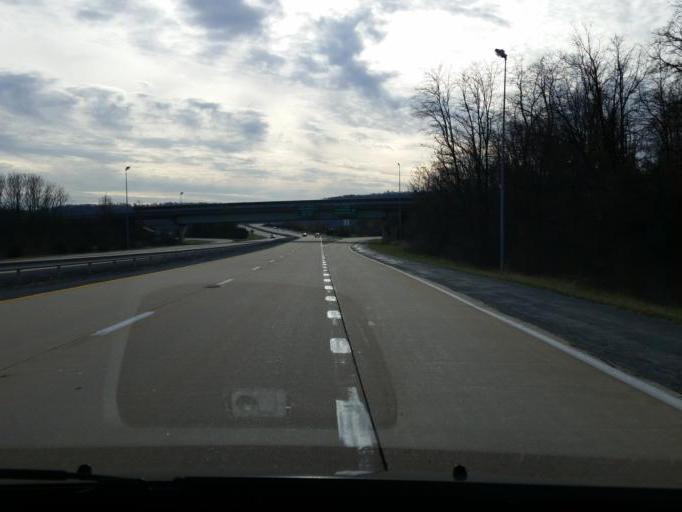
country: US
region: Pennsylvania
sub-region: Dauphin County
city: Middletown
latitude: 40.2051
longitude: -76.7567
